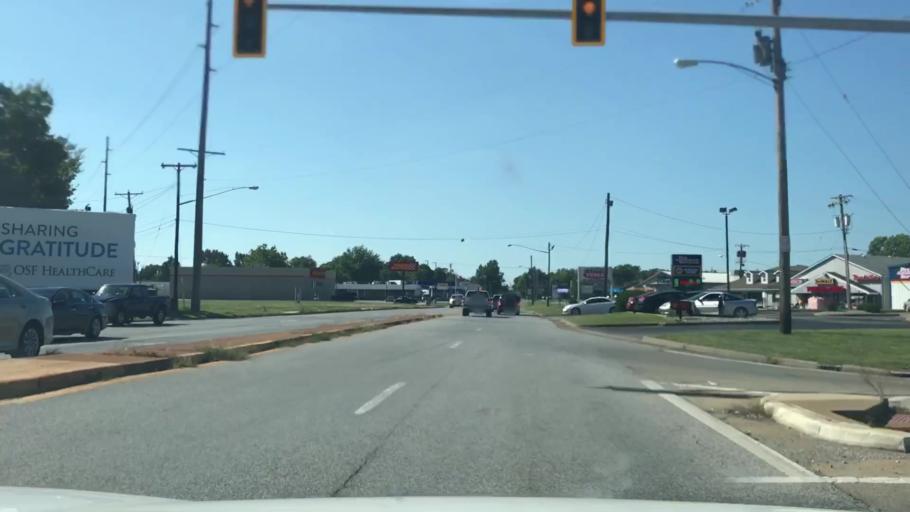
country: US
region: Illinois
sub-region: Madison County
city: Roxana
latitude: 38.8638
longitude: -90.0792
